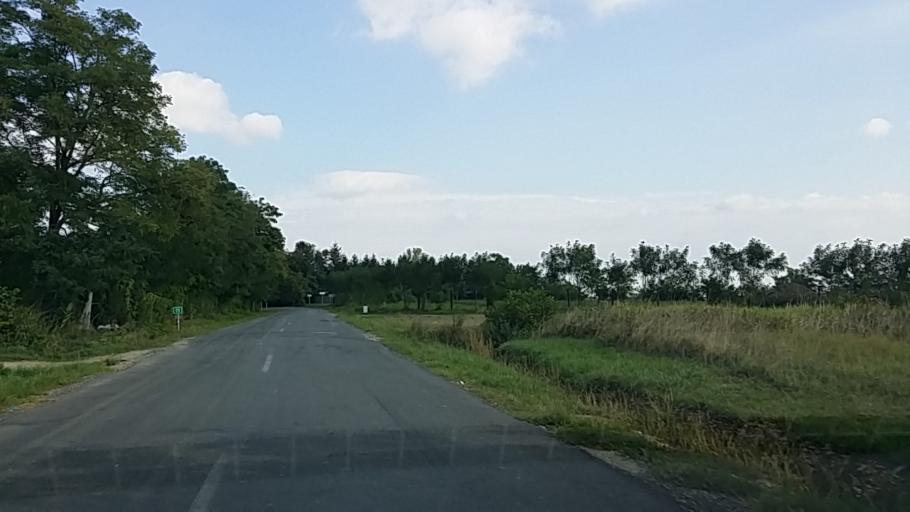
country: HU
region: Vas
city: Csepreg
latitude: 47.3887
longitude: 16.7160
